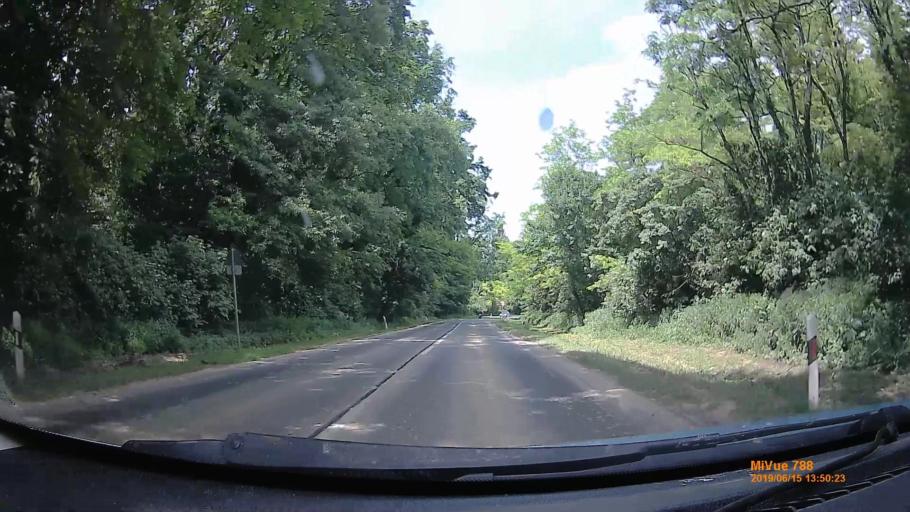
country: HU
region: Tolna
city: Iregszemcse
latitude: 46.7422
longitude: 18.1618
